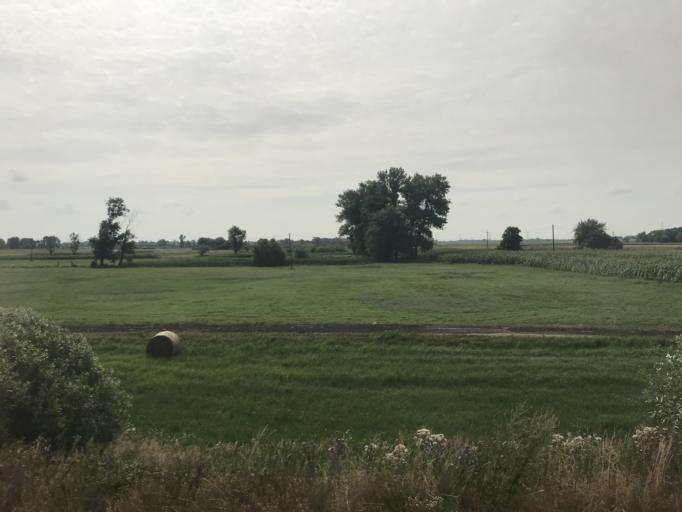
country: PL
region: Kujawsko-Pomorskie
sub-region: Powiat inowroclawski
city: Janikowo
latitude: 52.7747
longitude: 18.1553
